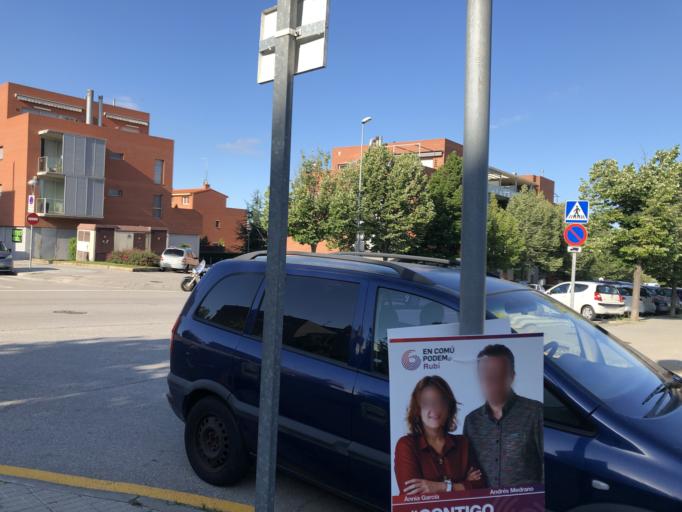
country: ES
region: Catalonia
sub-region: Provincia de Barcelona
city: Rubi
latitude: 41.4901
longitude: 2.0412
